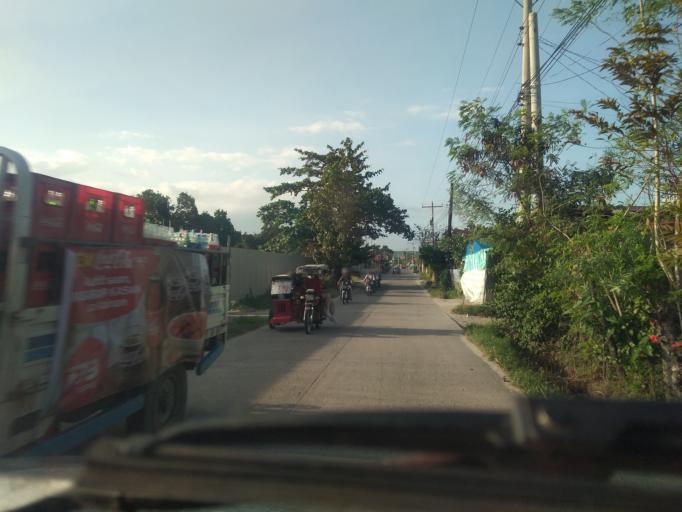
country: PH
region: Central Luzon
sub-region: Province of Pampanga
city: Bulaon
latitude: 15.0978
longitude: 120.6804
